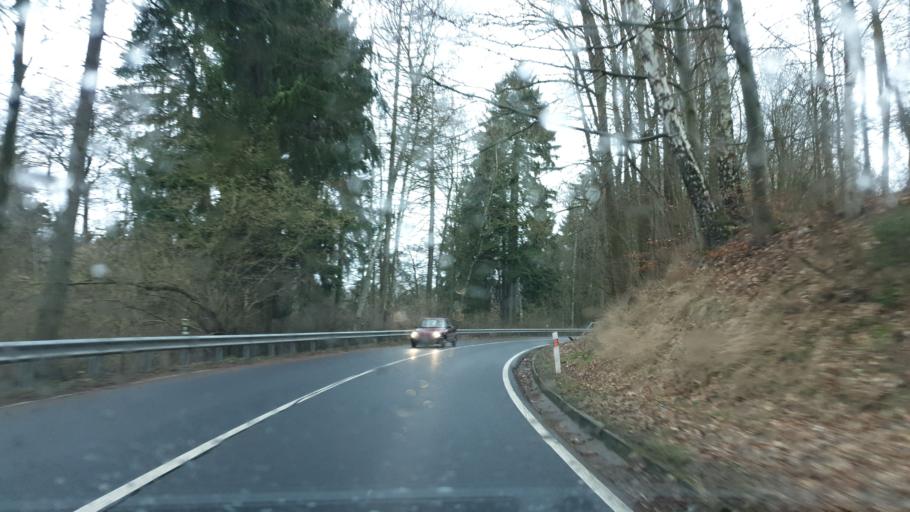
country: CZ
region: Karlovarsky
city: As
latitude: 50.2415
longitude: 12.1846
